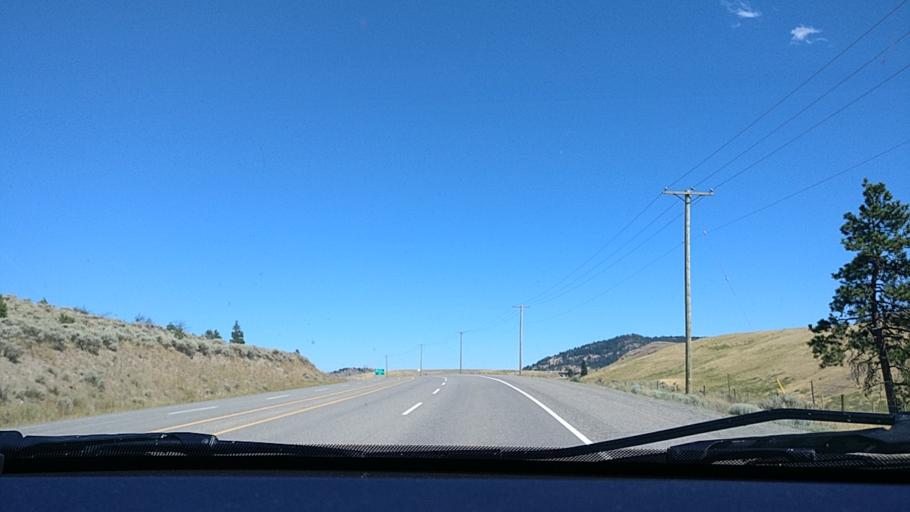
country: CA
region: British Columbia
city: Kamloops
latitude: 50.6689
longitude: -120.4769
